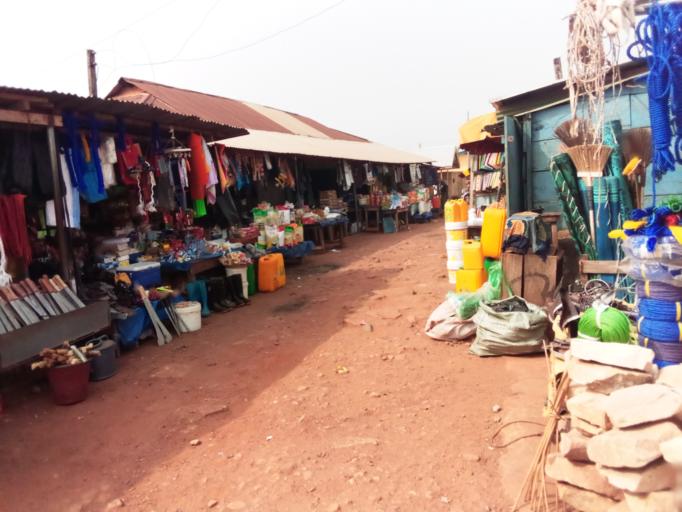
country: CI
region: Sud-Comoe
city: Ayame
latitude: 5.8222
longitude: -2.8204
